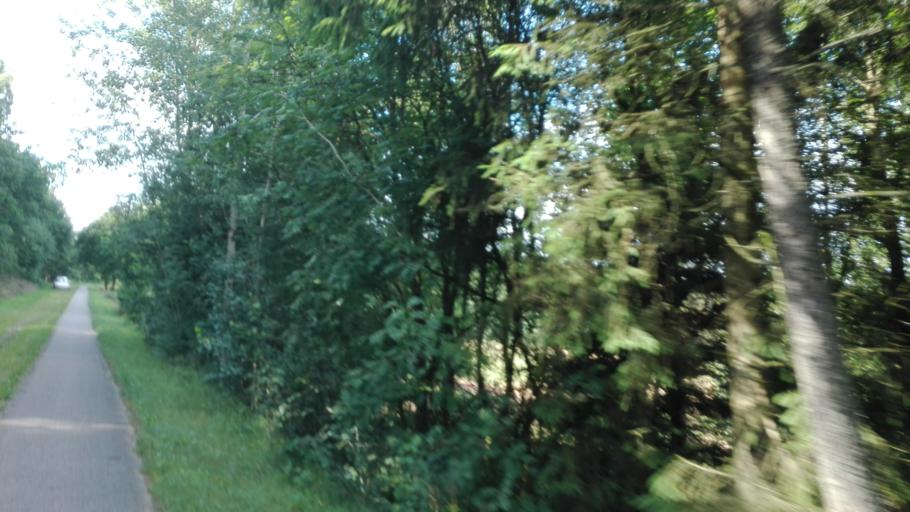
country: DK
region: Central Jutland
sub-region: Silkeborg Kommune
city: Virklund
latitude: 56.0447
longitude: 9.4708
